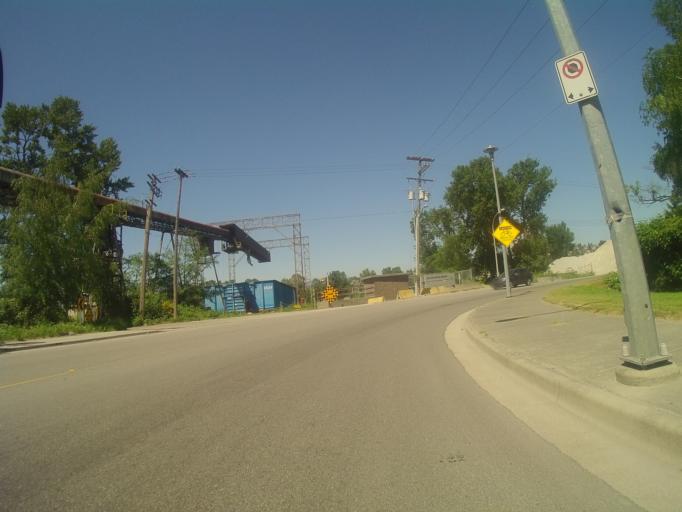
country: CA
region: British Columbia
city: Vancouver
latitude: 49.2012
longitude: -123.0693
